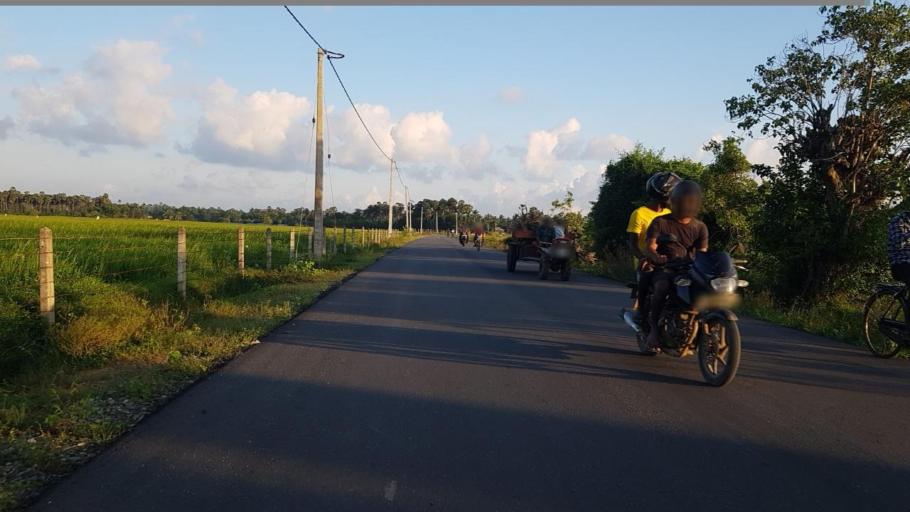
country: LK
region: Northern Province
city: Jaffna
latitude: 9.7258
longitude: 79.9751
